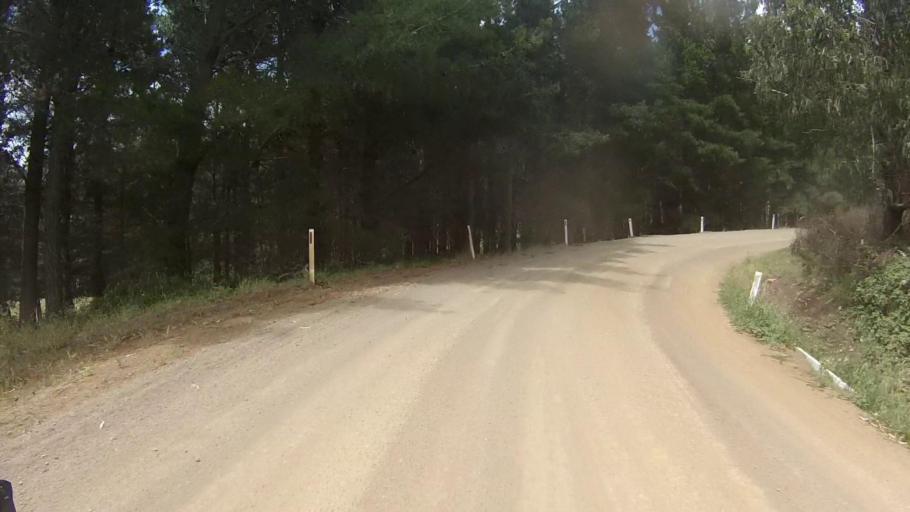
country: AU
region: Tasmania
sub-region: Sorell
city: Sorell
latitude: -42.8108
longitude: 147.8304
